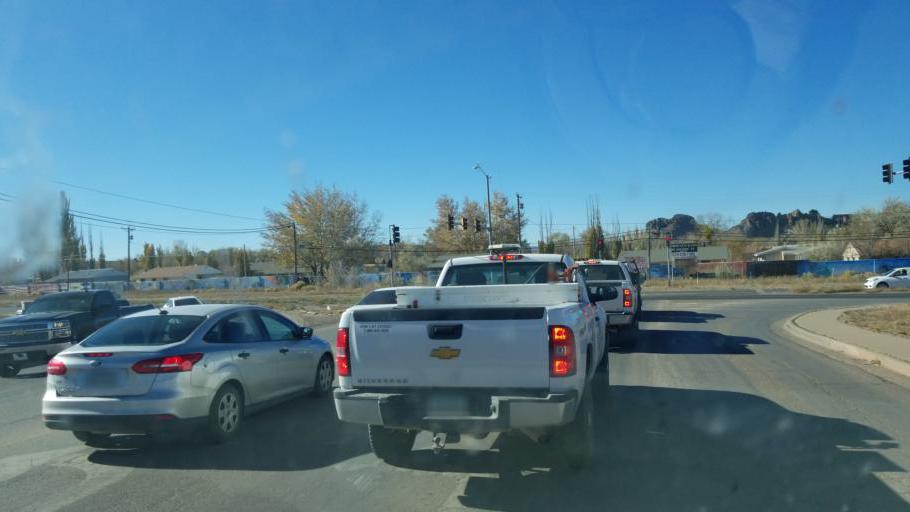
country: US
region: Arizona
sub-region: Apache County
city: Fort Defiance
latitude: 35.7346
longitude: -109.0590
